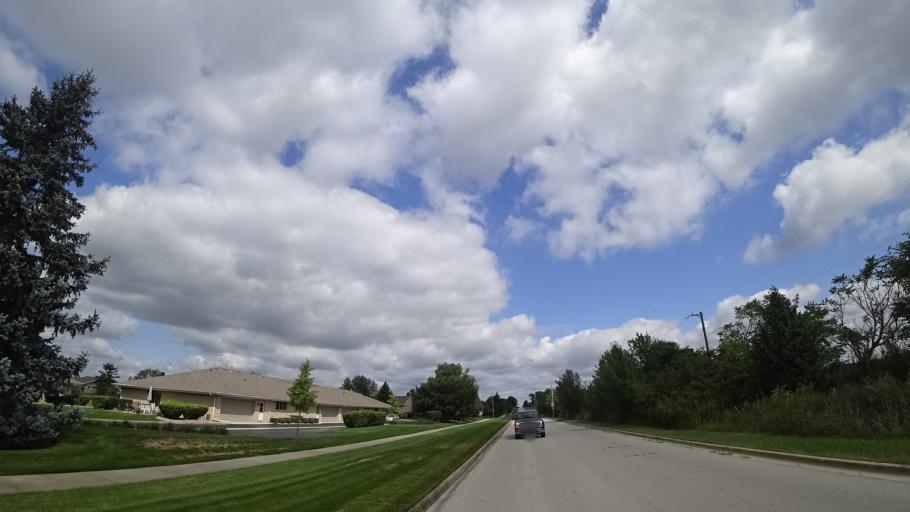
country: US
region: Illinois
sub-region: Will County
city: Mokena
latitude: 41.5575
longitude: -87.8708
